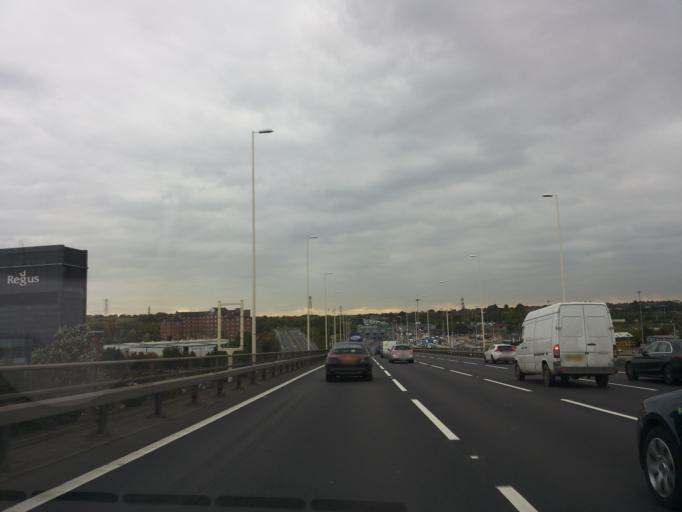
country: GB
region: England
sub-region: Kent
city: Stone
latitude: 51.4568
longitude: 0.2495
